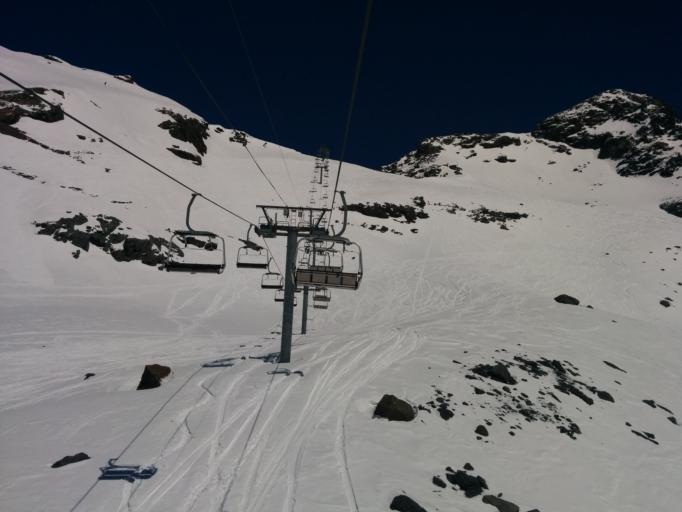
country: FR
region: Rhone-Alpes
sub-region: Departement de la Savoie
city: Val Thorens
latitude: 45.2539
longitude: 6.5956
